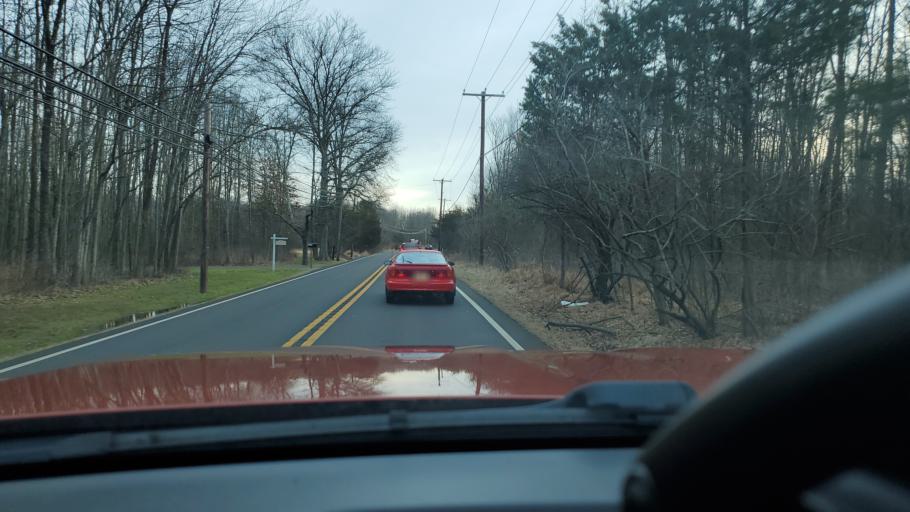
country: US
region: Pennsylvania
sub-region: Bucks County
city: Sellersville
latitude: 40.3602
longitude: -75.3455
